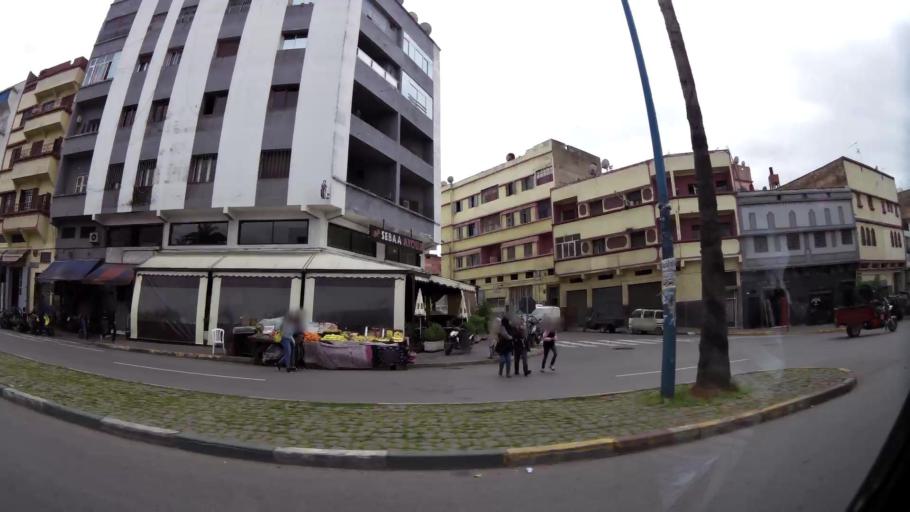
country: MA
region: Grand Casablanca
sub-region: Casablanca
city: Casablanca
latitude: 33.5831
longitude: -7.5544
